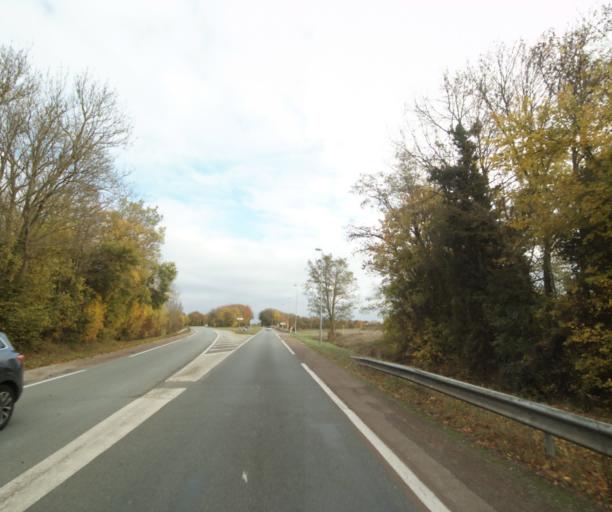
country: FR
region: Poitou-Charentes
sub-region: Departement de la Charente-Maritime
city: Saintes
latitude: 45.7575
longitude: -0.6614
